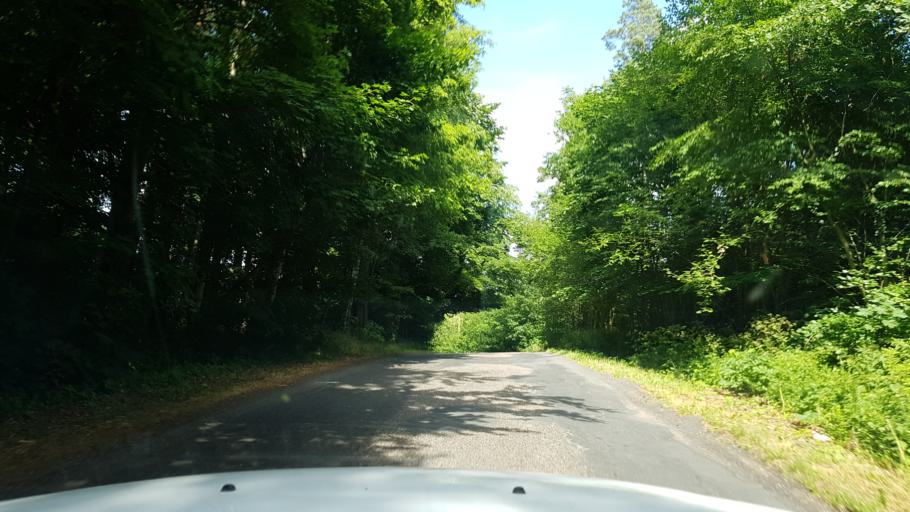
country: PL
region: West Pomeranian Voivodeship
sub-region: Powiat goleniowski
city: Mosty
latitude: 53.5514
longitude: 14.9626
